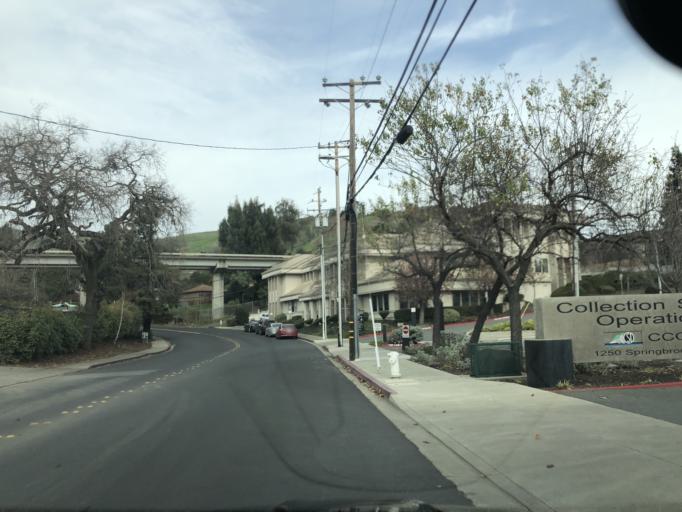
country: US
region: California
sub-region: Contra Costa County
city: Saranap
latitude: 37.8973
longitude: -122.0738
